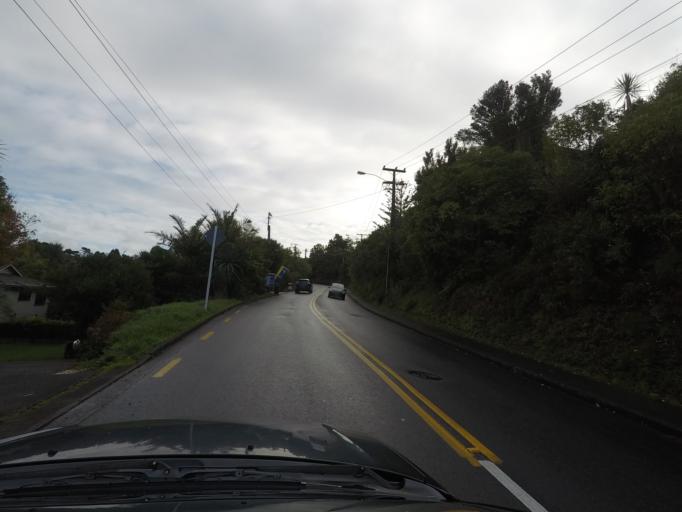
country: NZ
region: Auckland
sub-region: Auckland
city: Rothesay Bay
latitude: -36.7113
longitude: 174.7444
